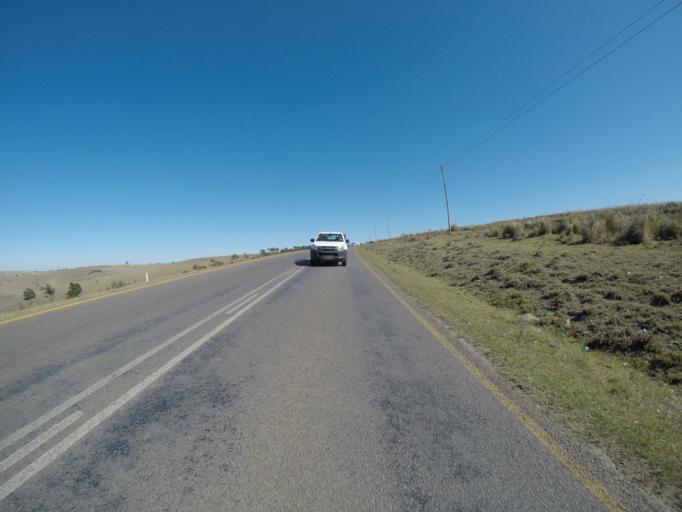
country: ZA
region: Eastern Cape
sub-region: OR Tambo District Municipality
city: Mthatha
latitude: -31.8050
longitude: 28.7543
